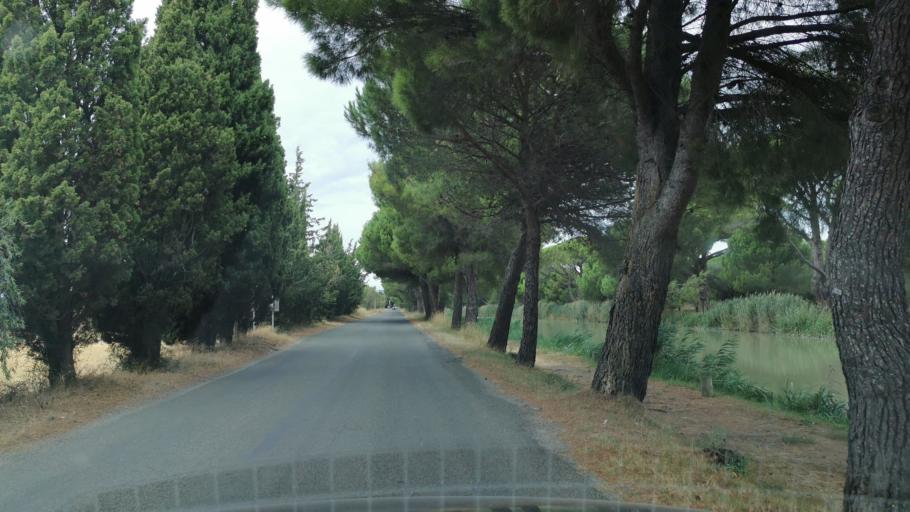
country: FR
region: Languedoc-Roussillon
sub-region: Departement de l'Aude
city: Saint-Marcel-sur-Aude
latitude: 43.2680
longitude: 2.9384
